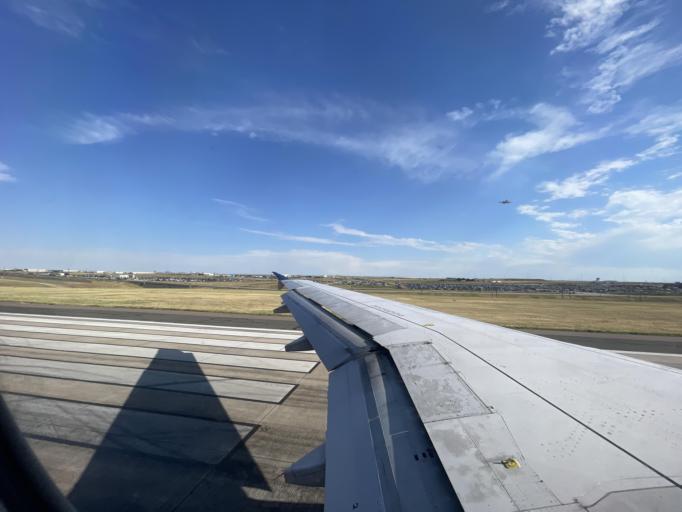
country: US
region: Colorado
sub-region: Weld County
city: Lochbuie
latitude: 39.8407
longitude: -104.6846
